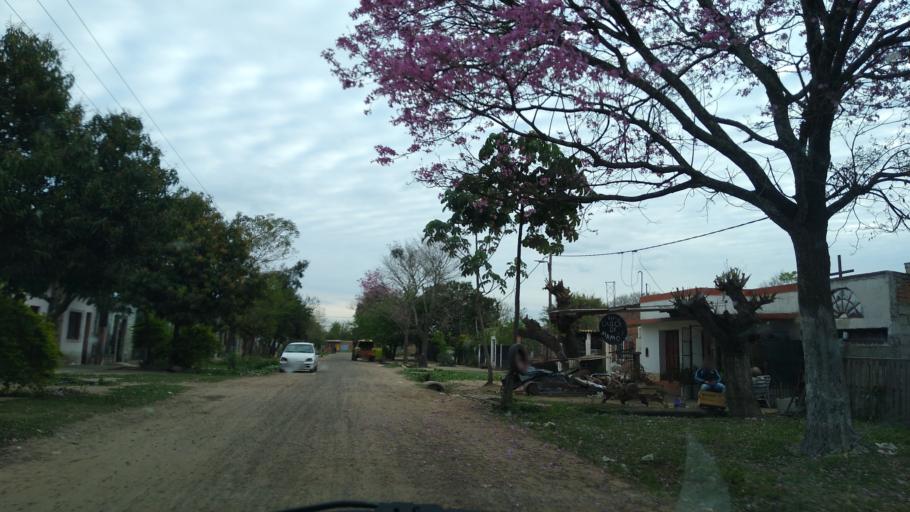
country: AR
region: Chaco
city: Fontana
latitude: -27.4011
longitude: -59.0395
